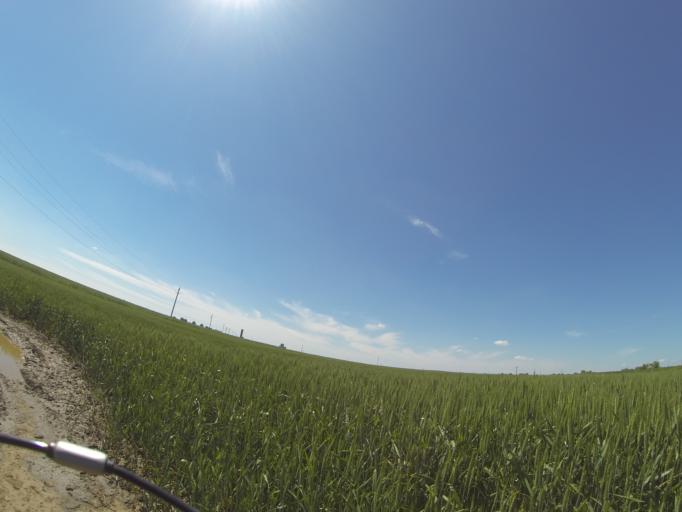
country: RO
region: Dolj
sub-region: Comuna Leu
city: Zanoaga
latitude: 44.2009
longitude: 24.0642
